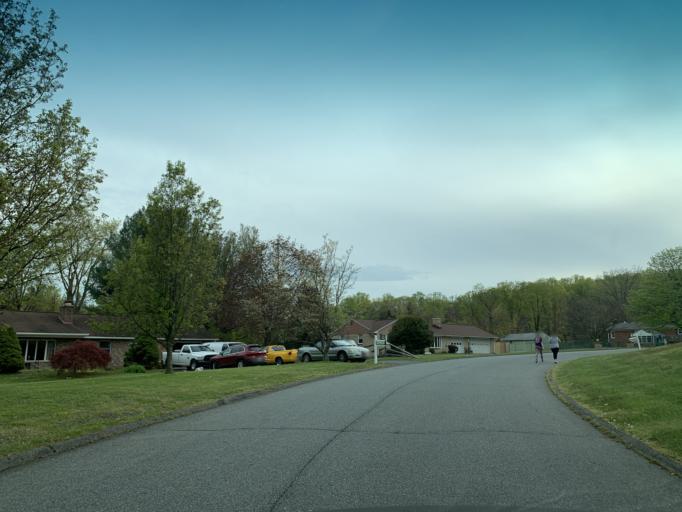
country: US
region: Maryland
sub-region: Harford County
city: Pleasant Hills
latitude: 39.4947
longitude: -76.3712
